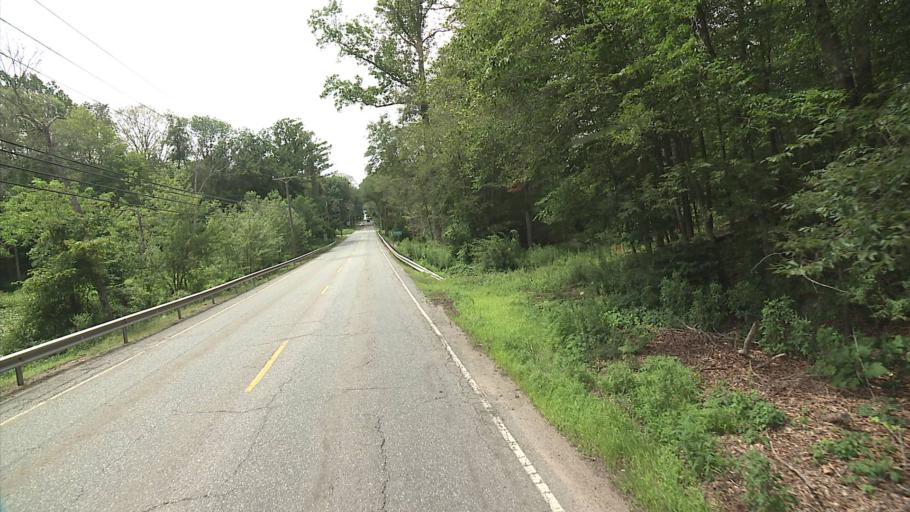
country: US
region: Connecticut
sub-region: Middlesex County
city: Chester Center
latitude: 41.3595
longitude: -72.4981
